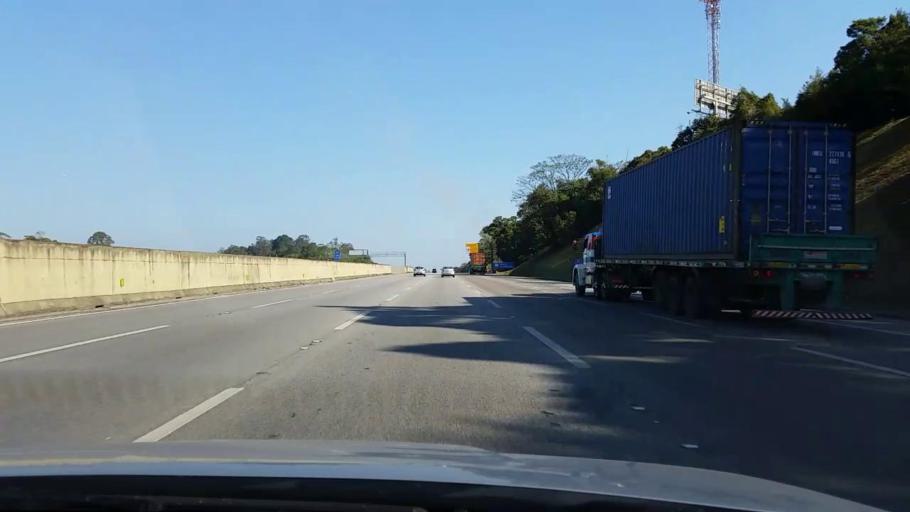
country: BR
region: Sao Paulo
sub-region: Sao Bernardo Do Campo
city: Sao Bernardo do Campo
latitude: -23.7746
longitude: -46.5948
